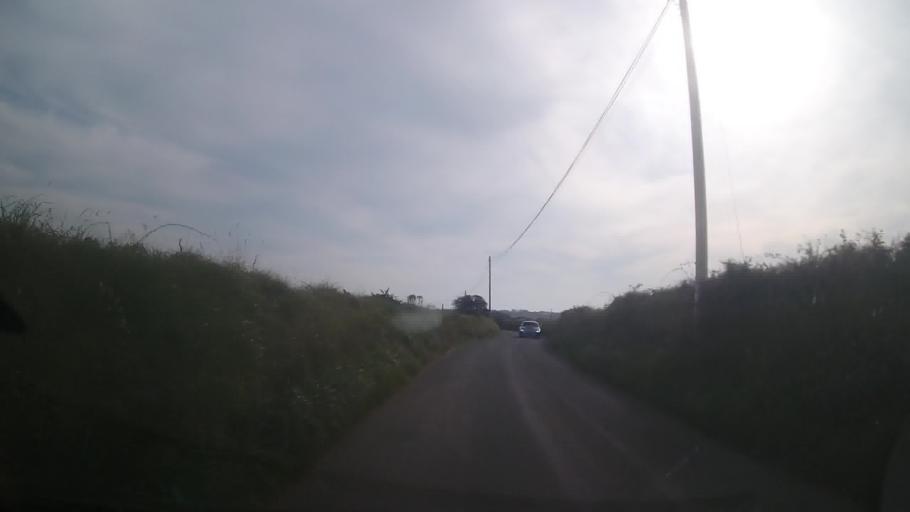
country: GB
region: Wales
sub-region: Pembrokeshire
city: Saint David's
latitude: 51.9037
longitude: -5.2448
